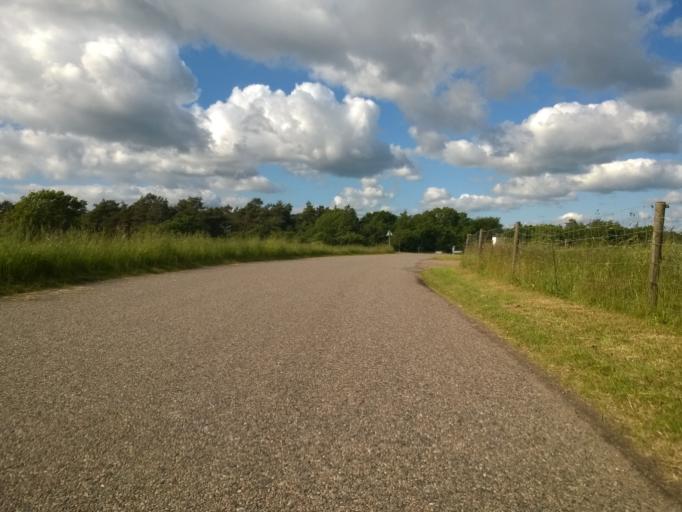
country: DK
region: Central Jutland
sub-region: Holstebro Kommune
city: Vinderup
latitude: 56.4789
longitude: 8.8636
